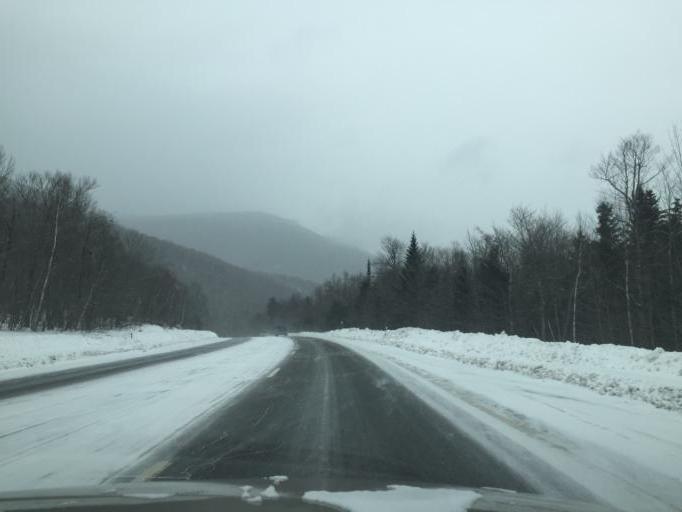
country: US
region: New Hampshire
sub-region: Coos County
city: Gorham
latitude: 44.2193
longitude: -71.2498
